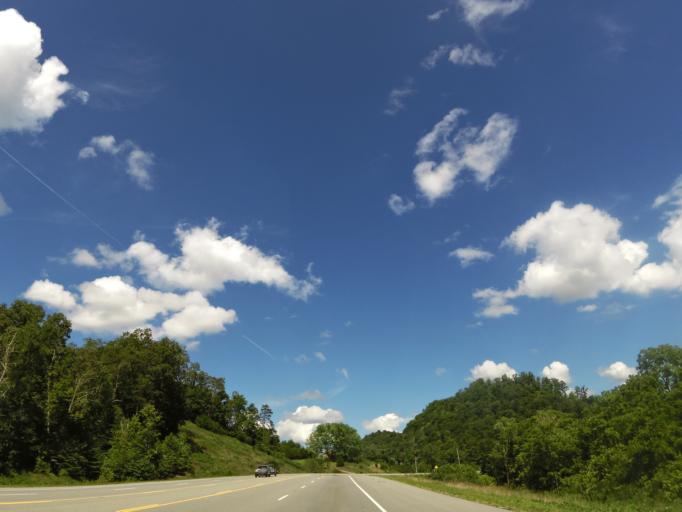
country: US
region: Tennessee
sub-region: Claiborne County
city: Tazewell
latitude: 36.4087
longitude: -83.4783
